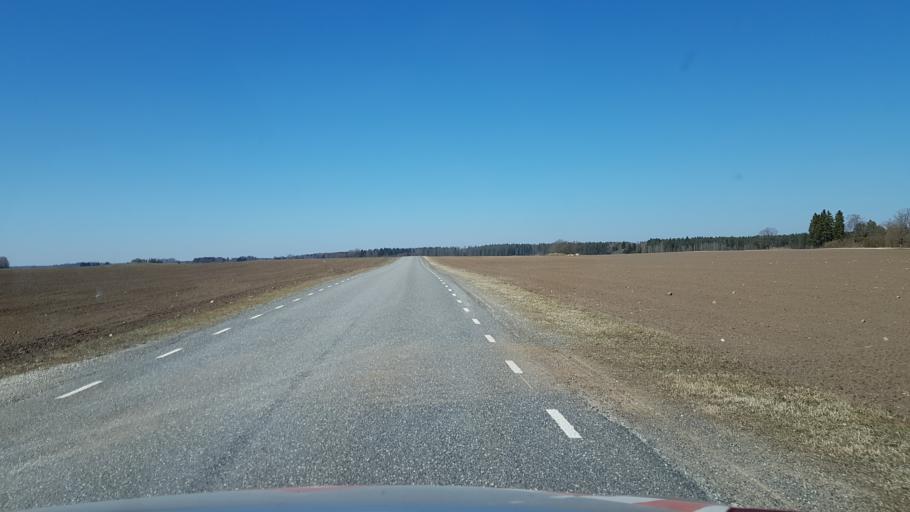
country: EE
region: Laeaene-Virumaa
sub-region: Rakke vald
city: Rakke
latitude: 59.0045
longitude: 26.1860
